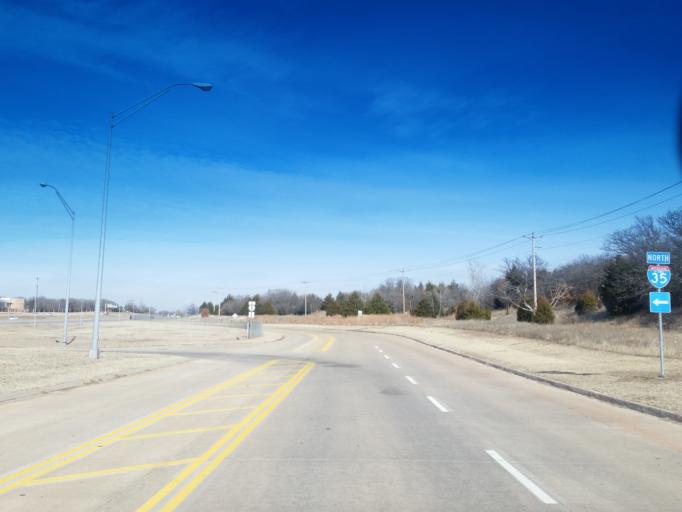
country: US
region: Oklahoma
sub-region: Oklahoma County
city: Edmond
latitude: 35.6241
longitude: -97.4235
